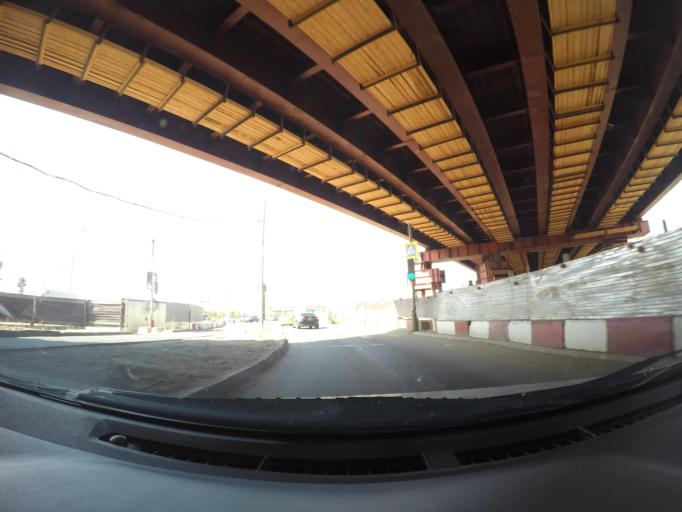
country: RU
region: Moscow
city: Likhobory
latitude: 55.8376
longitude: 37.5711
